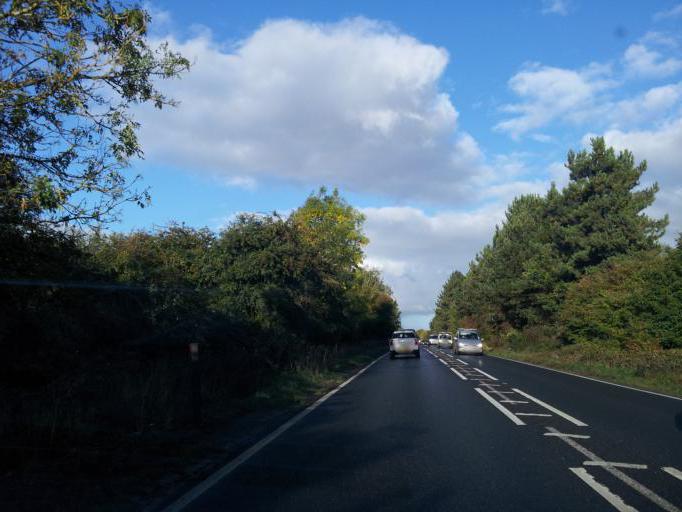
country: GB
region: England
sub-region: Norfolk
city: Mattishall
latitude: 52.6654
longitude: 1.1064
